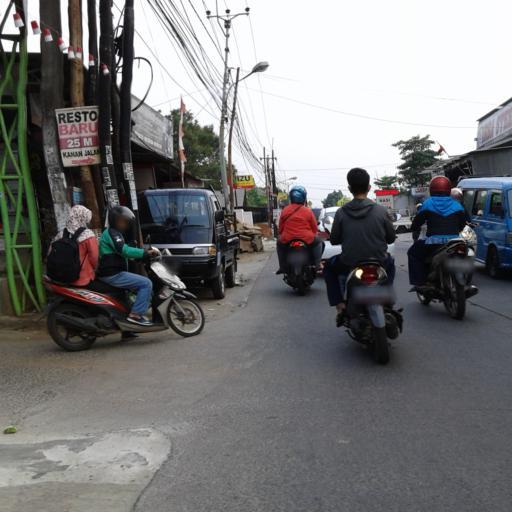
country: ID
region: West Java
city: Sawangan
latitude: -6.3870
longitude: 106.7688
